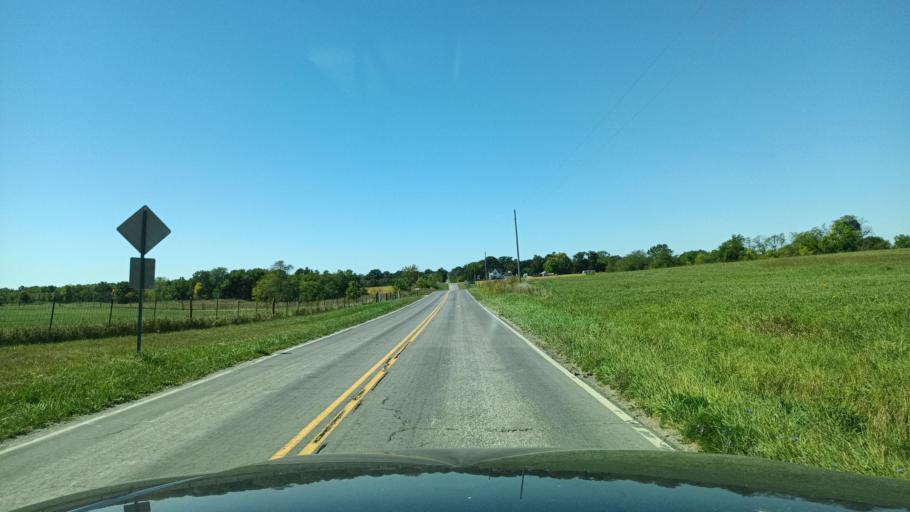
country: US
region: Missouri
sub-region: Macon County
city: La Plata
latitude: 40.0231
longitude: -92.5814
